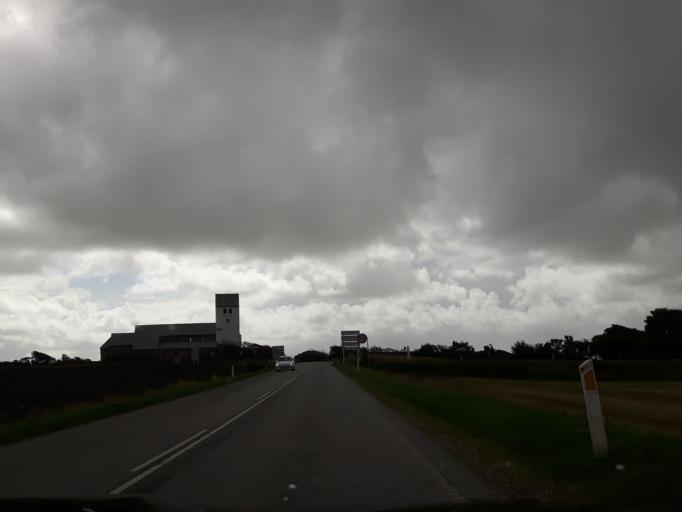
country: DK
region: North Denmark
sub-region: Thisted Kommune
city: Hurup
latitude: 56.7760
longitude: 8.3175
